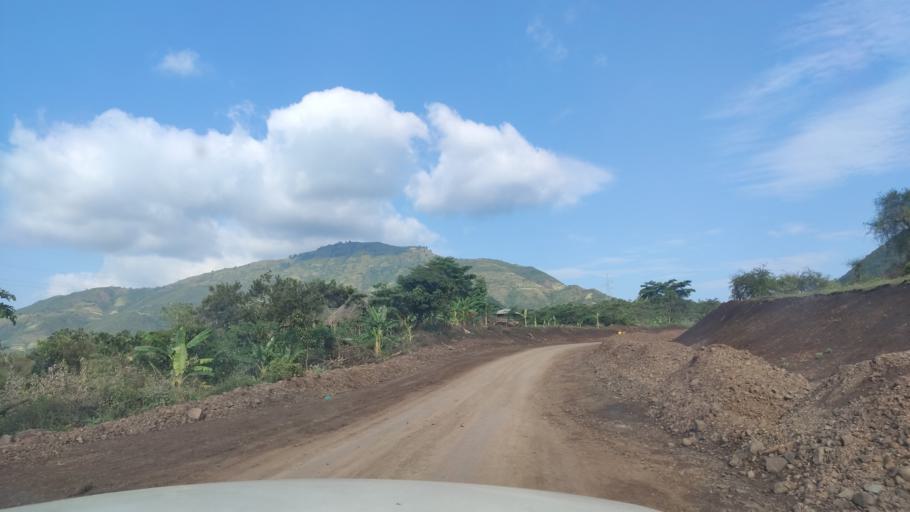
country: ET
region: Southern Nations, Nationalities, and People's Region
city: Arba Minch'
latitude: 6.4272
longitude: 37.3269
